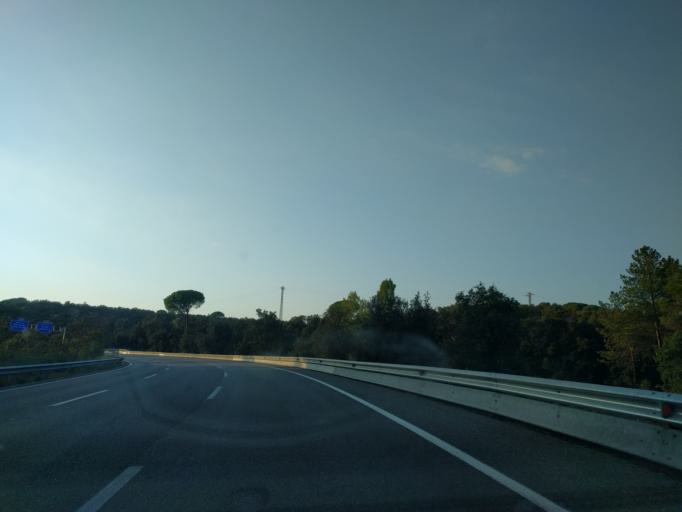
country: ES
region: Catalonia
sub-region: Provincia de Girona
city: Llagostera
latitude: 41.8304
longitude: 2.9372
